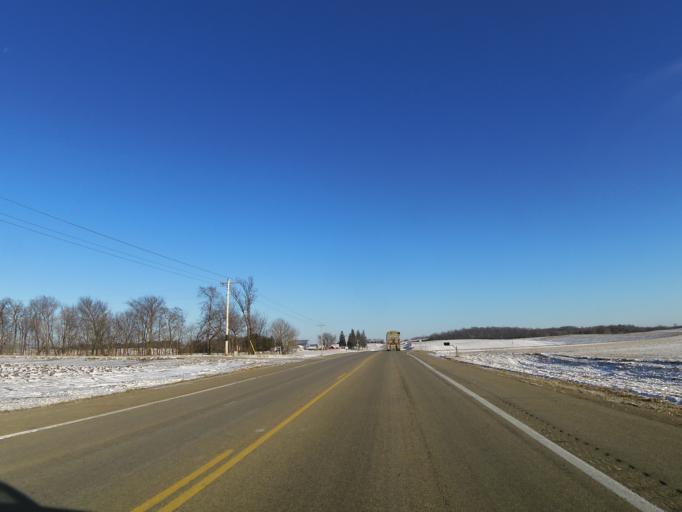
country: US
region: Minnesota
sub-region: Rice County
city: Lonsdale
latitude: 44.4862
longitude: -93.4660
